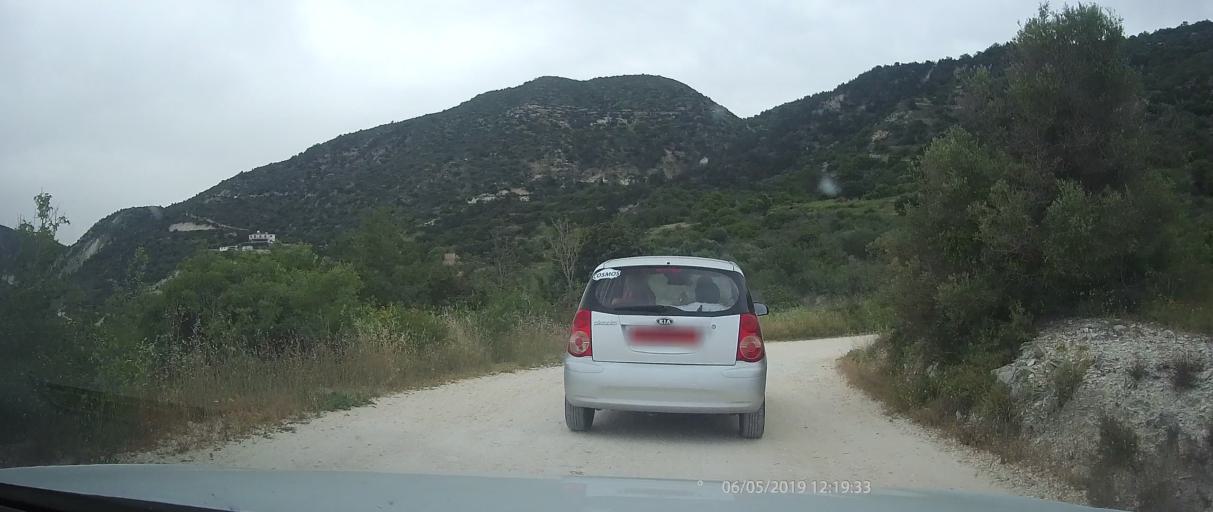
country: CY
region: Pafos
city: Tala
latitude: 34.8603
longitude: 32.4286
